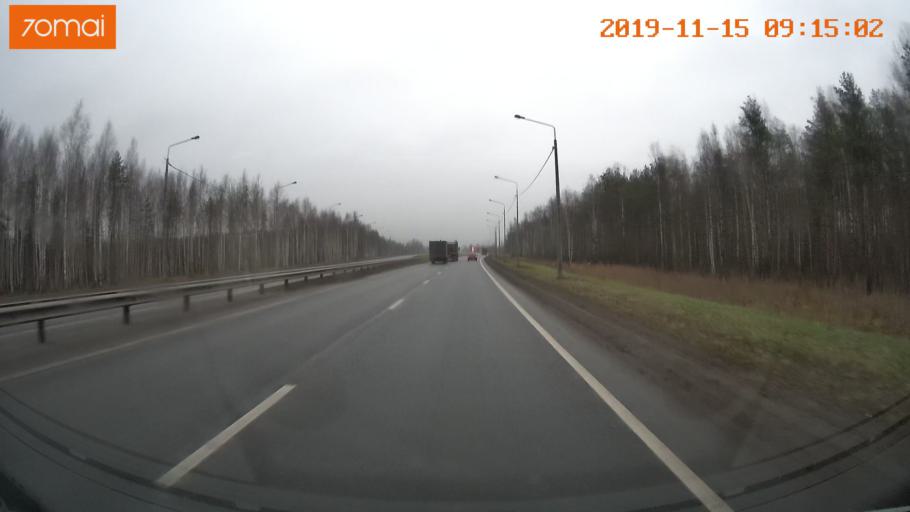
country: RU
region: Vologda
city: Tonshalovo
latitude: 59.2340
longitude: 37.9639
